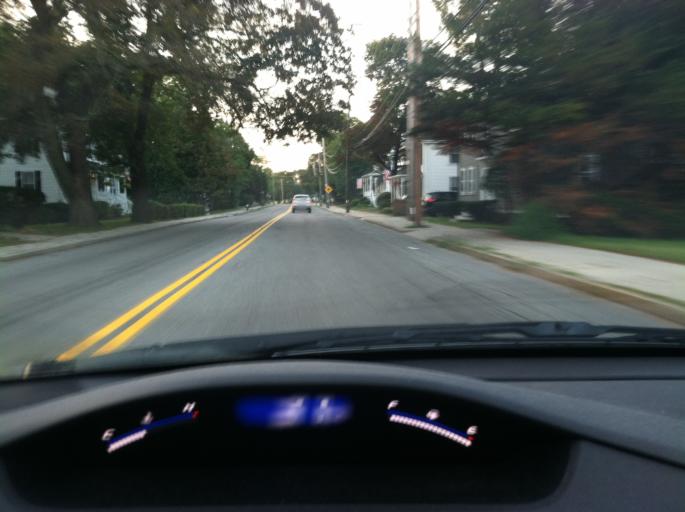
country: US
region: Massachusetts
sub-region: Middlesex County
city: Lexington
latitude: 42.4574
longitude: -71.2365
